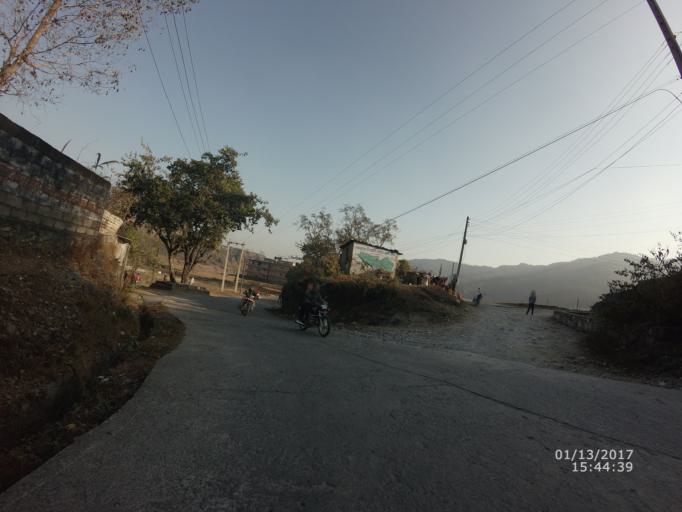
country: NP
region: Western Region
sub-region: Gandaki Zone
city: Pokhara
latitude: 28.1765
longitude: 83.9920
